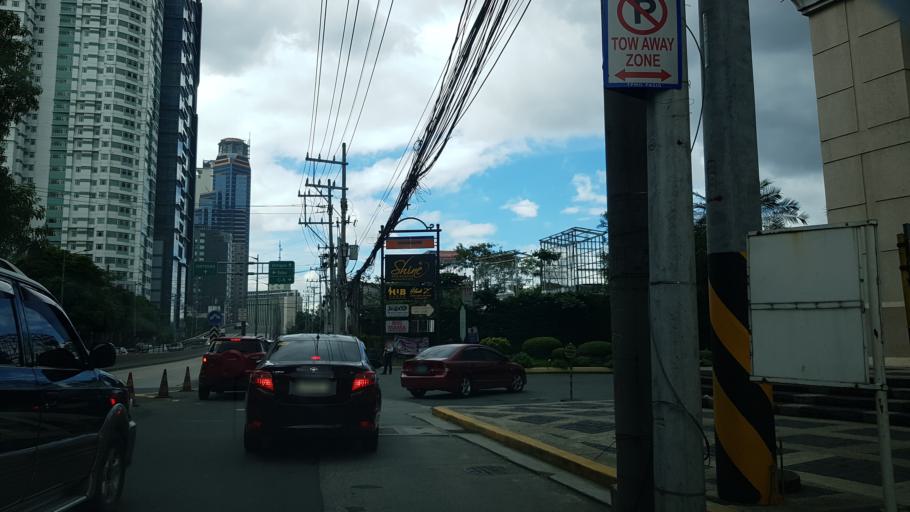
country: PH
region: Metro Manila
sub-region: Pasig
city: Pasig City
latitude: 14.5814
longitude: 121.0639
